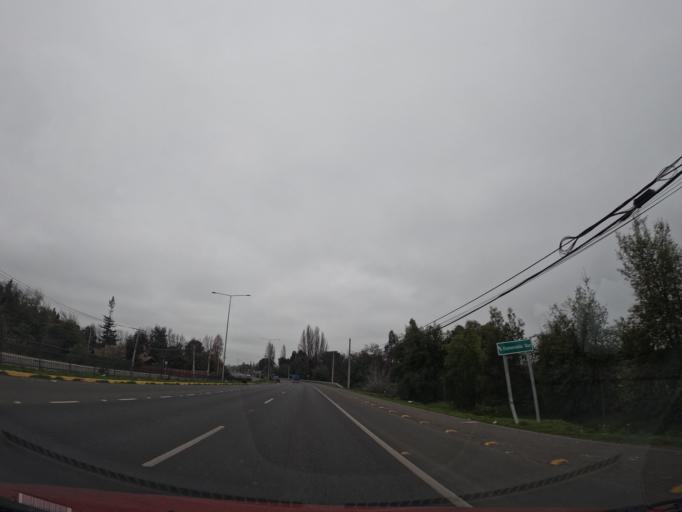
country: CL
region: Maule
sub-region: Provincia de Talca
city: Talca
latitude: -35.4477
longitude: -71.6017
